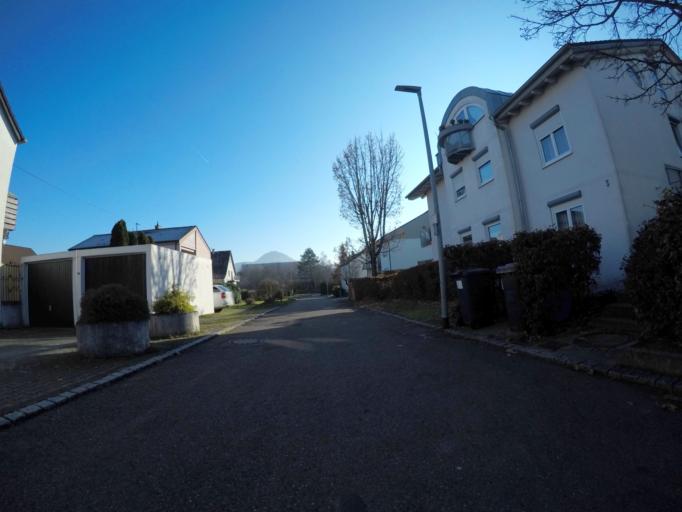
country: DE
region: Baden-Wuerttemberg
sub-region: Tuebingen Region
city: Reutlingen
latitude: 48.5141
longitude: 9.2216
